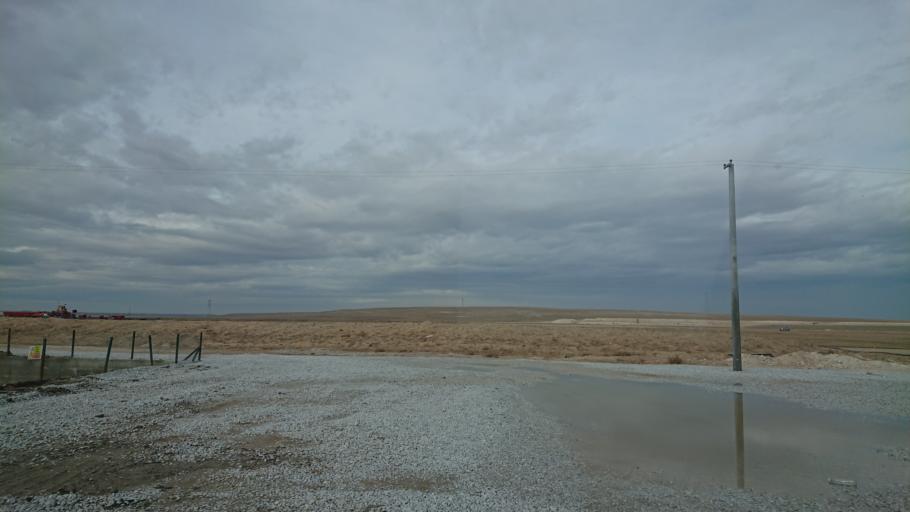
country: TR
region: Aksaray
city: Sultanhani
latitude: 38.1324
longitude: 33.5533
